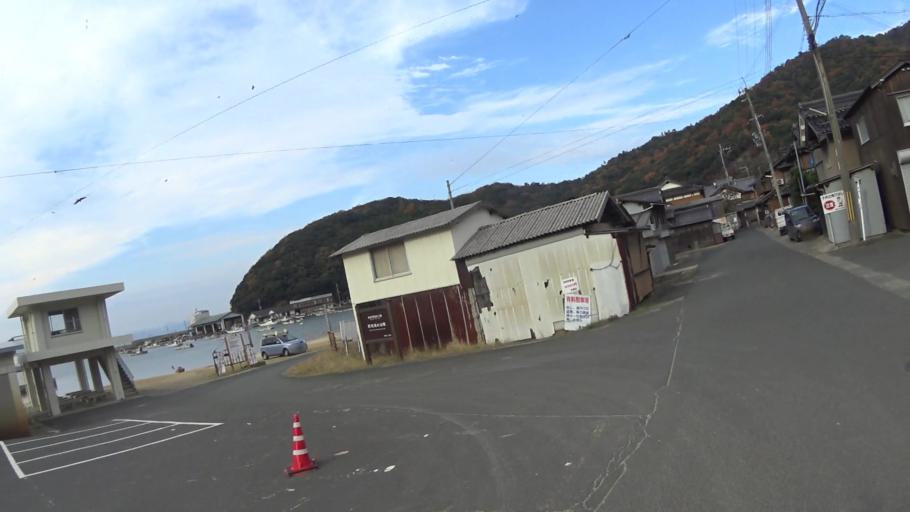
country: JP
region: Kyoto
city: Maizuru
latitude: 35.5680
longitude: 135.4281
